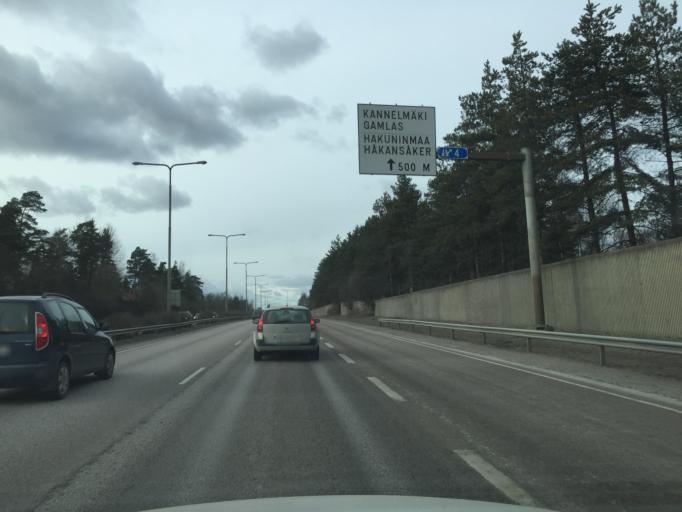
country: FI
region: Uusimaa
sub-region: Helsinki
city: Teekkarikylae
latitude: 60.2422
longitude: 24.8937
